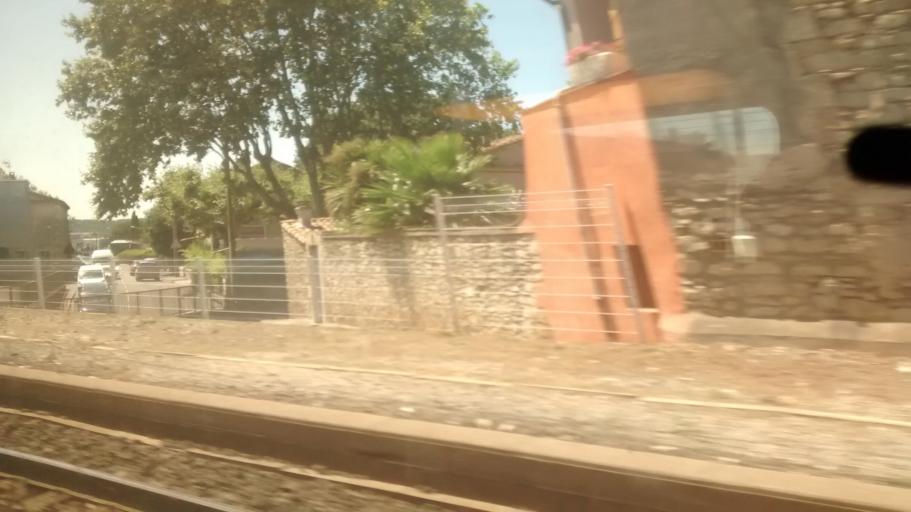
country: FR
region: Languedoc-Roussillon
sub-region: Departement du Gard
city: Nimes
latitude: 43.8138
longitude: 4.3285
